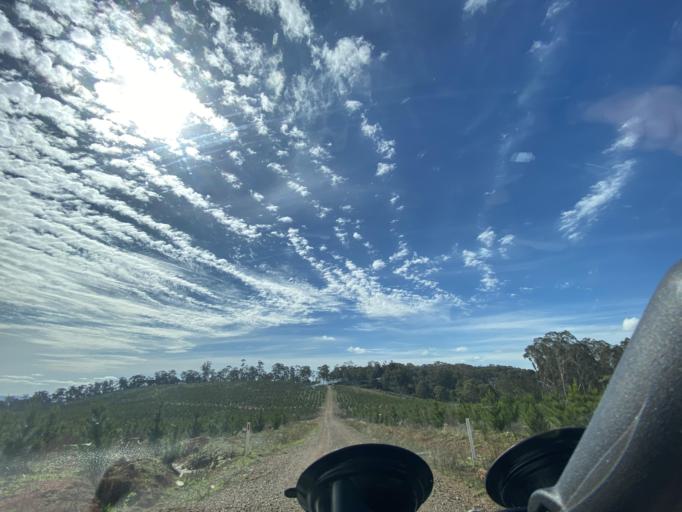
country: AU
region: Victoria
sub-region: Mansfield
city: Mansfield
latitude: -36.8214
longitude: 146.1029
